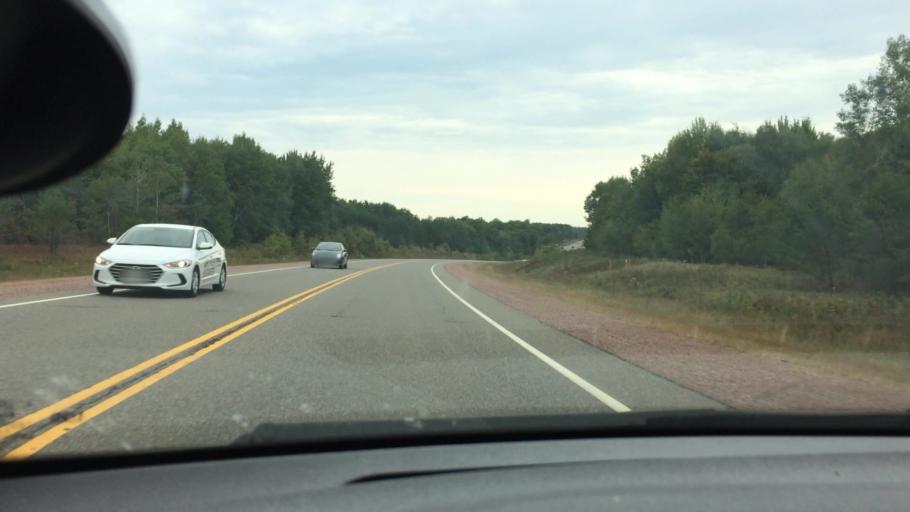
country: US
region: Wisconsin
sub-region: Clark County
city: Neillsville
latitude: 44.5679
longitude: -90.7231
